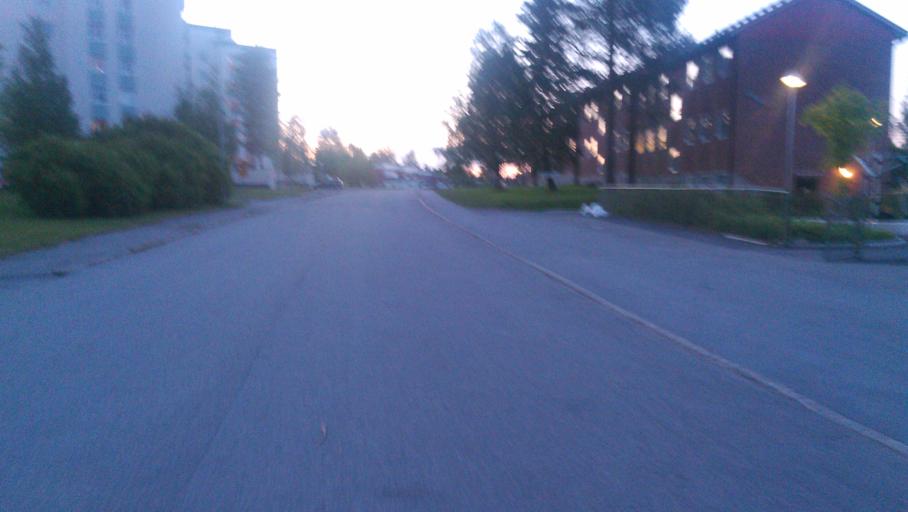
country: SE
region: Vaesterbotten
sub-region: Umea Kommun
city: Umea
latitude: 63.8270
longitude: 20.3018
